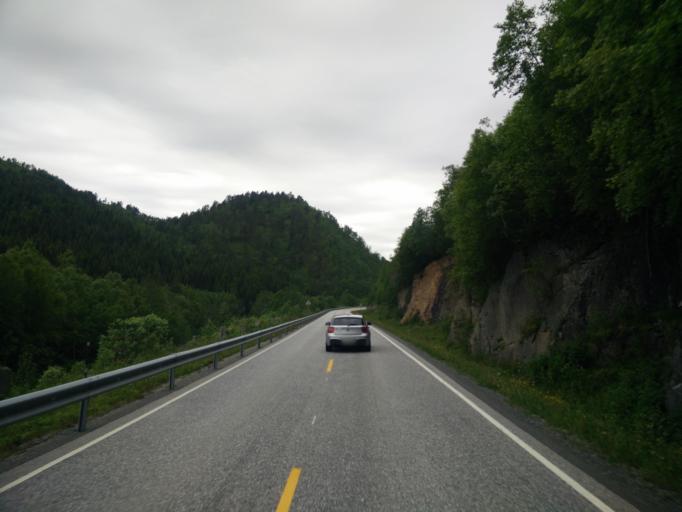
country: NO
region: Sor-Trondelag
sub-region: Hemne
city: Kyrksaeterora
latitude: 63.2106
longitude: 9.1526
